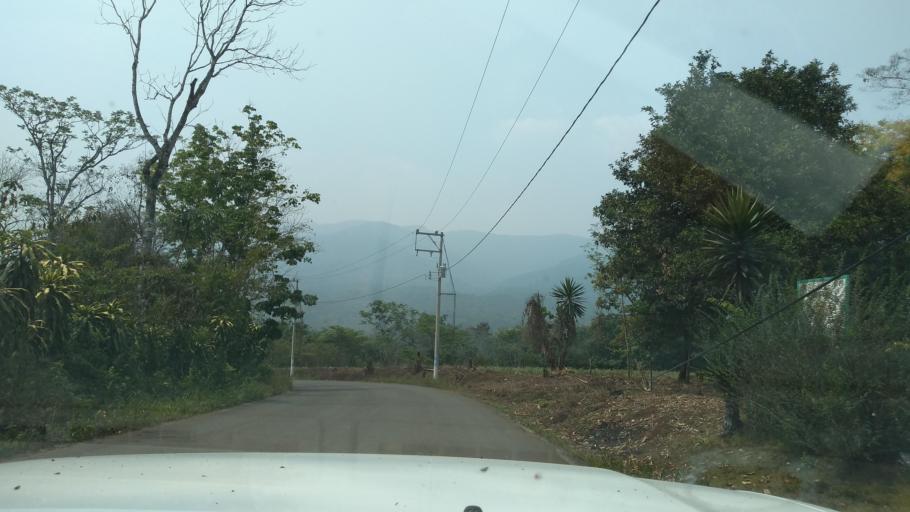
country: MX
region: Veracruz
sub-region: Tezonapa
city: Laguna Chica (Pueblo Nuevo)
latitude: 18.5428
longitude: -96.7700
